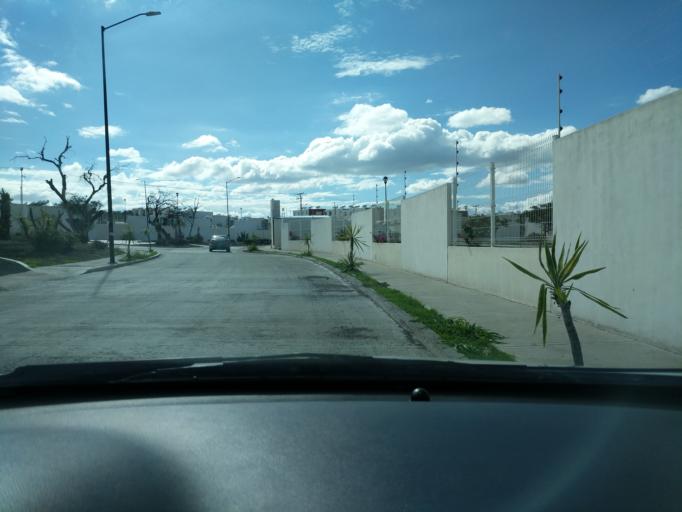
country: MX
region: Queretaro
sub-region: El Marques
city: La Loma
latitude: 20.5859
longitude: -100.2619
